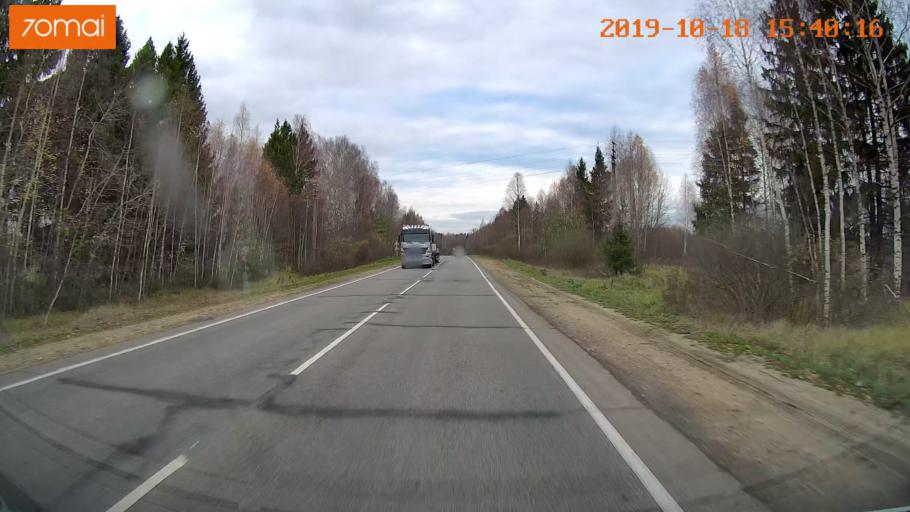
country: RU
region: Vladimir
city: Golovino
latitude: 55.9313
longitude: 40.5947
